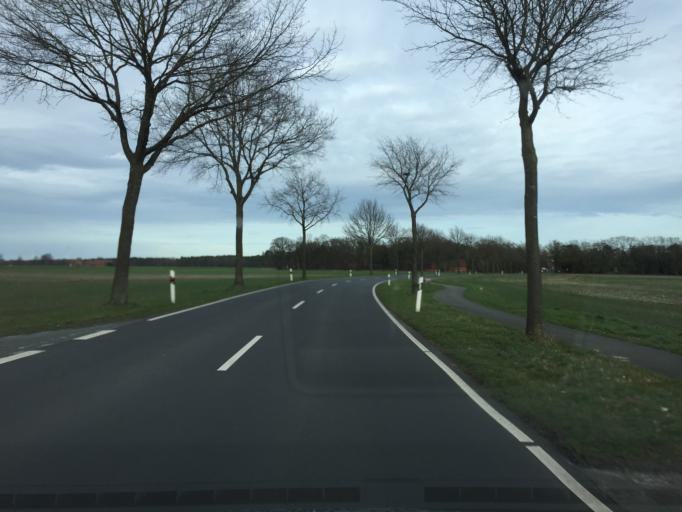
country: DE
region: Lower Saxony
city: Scholen
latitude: 52.6983
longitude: 8.7703
